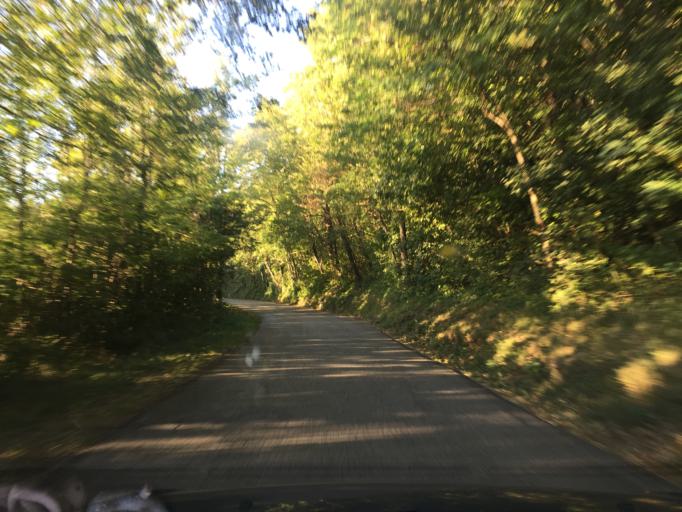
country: SI
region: Vipava
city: Vipava
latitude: 45.7941
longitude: 13.9937
